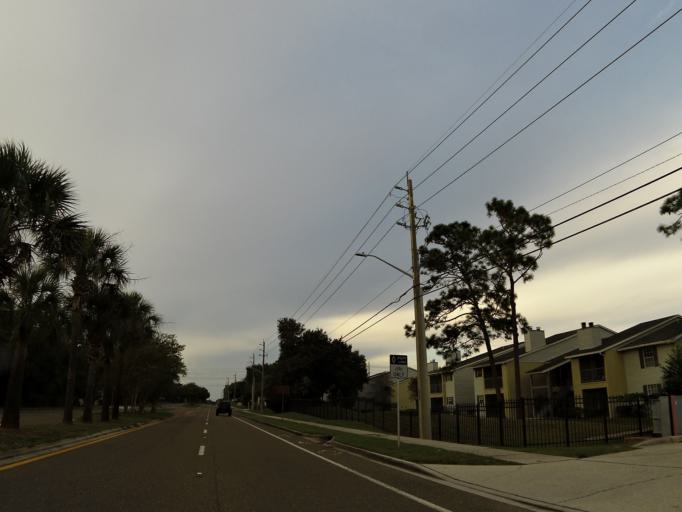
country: US
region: Florida
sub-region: Duval County
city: Atlantic Beach
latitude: 30.3649
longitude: -81.5028
